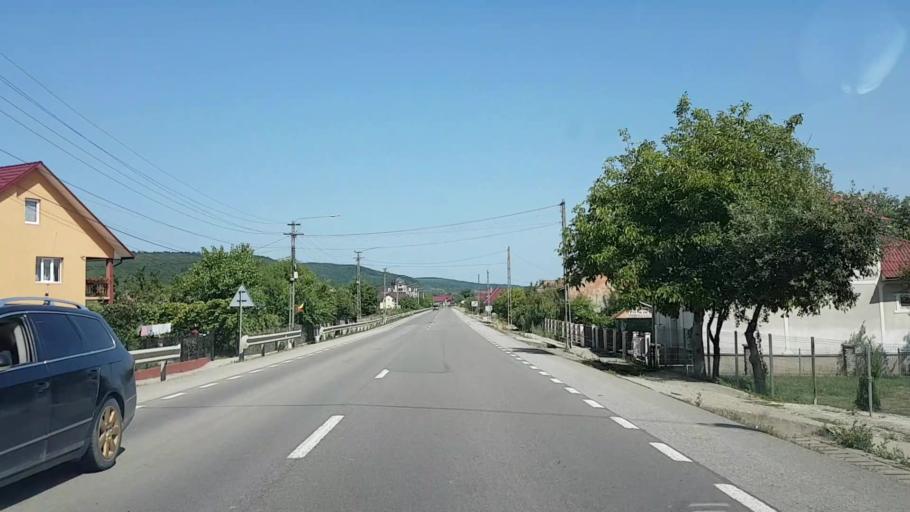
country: RO
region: Bistrita-Nasaud
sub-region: Comuna Uriu
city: Cristestii Ciceului
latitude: 47.1891
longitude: 24.1063
